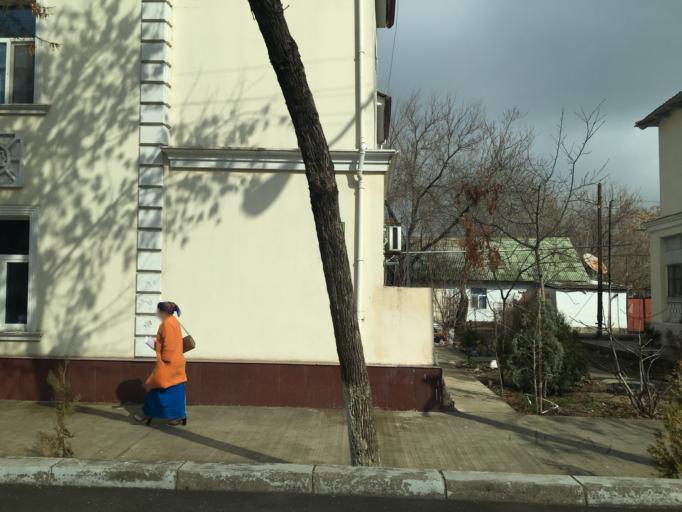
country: TM
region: Ahal
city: Ashgabat
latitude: 37.9454
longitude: 58.3631
